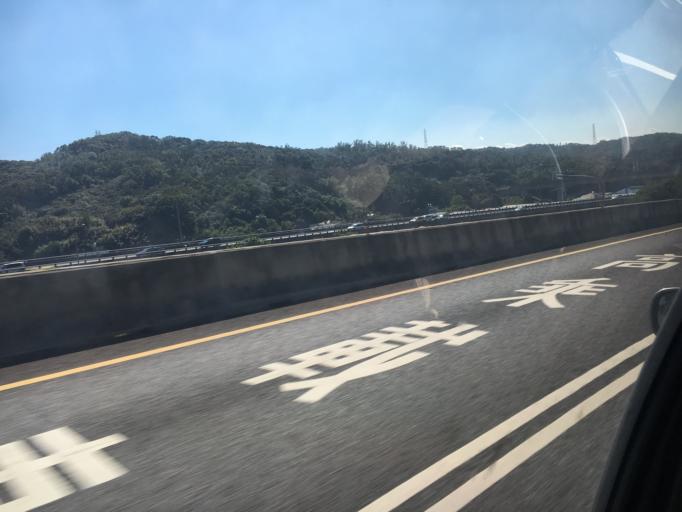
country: TW
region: Taiwan
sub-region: Taoyuan
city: Taoyuan
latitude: 25.0523
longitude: 121.3252
